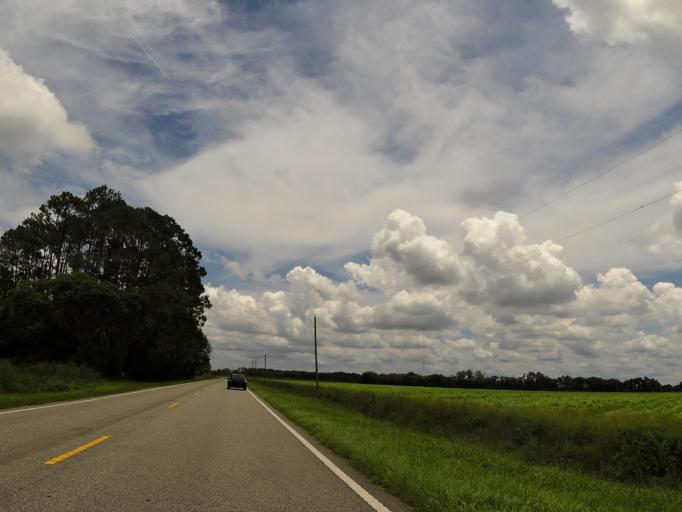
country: US
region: Florida
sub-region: Putnam County
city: East Palatka
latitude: 29.6985
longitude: -81.4950
